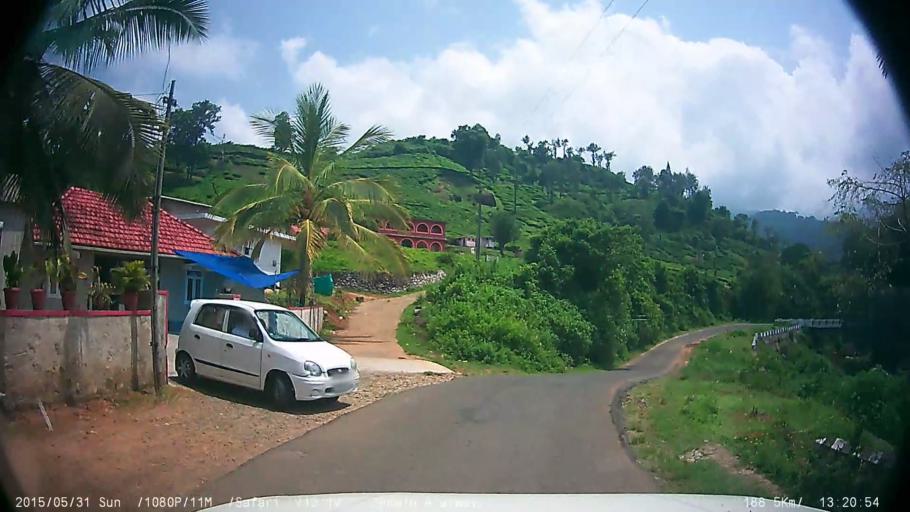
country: IN
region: Kerala
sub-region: Wayanad
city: Kalpetta
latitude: 11.5315
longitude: 76.1362
